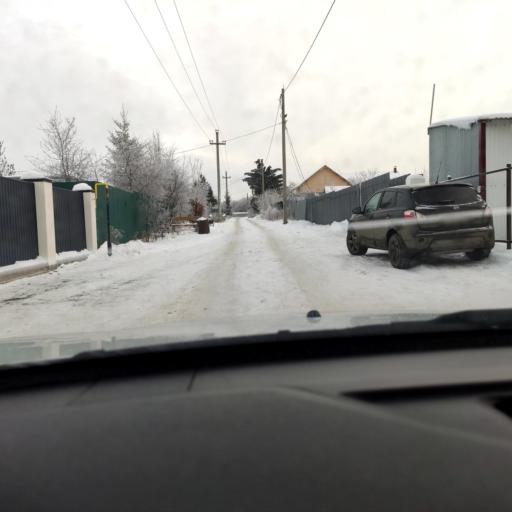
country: RU
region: Samara
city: Petra-Dubrava
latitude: 53.3016
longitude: 50.2496
